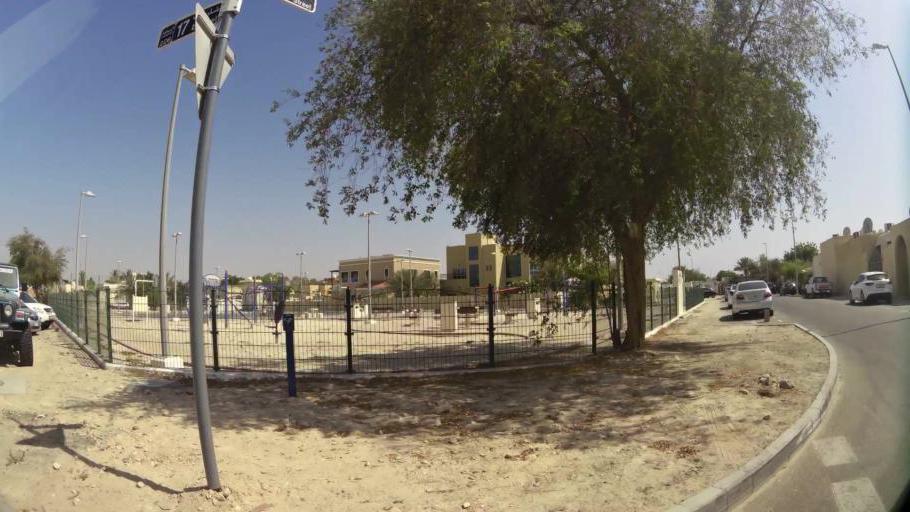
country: AE
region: Ash Shariqah
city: Sharjah
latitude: 25.2700
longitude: 55.3702
